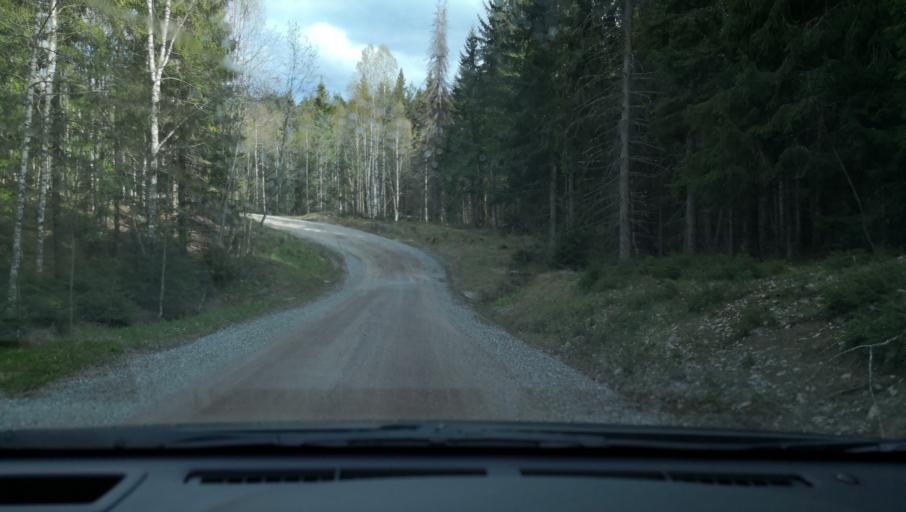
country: SE
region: Vaestmanland
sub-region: Fagersta Kommun
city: Fagersta
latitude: 60.1559
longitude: 15.6956
